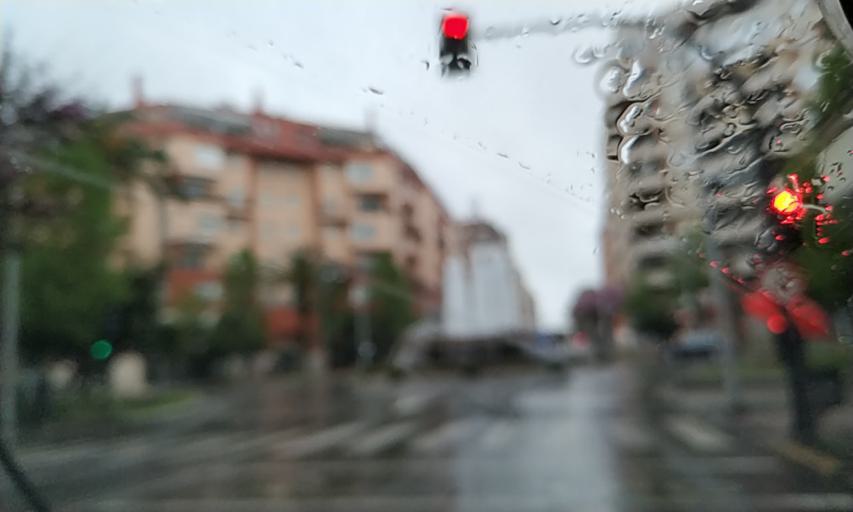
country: ES
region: Extremadura
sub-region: Provincia de Badajoz
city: Badajoz
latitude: 38.8735
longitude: -6.9728
